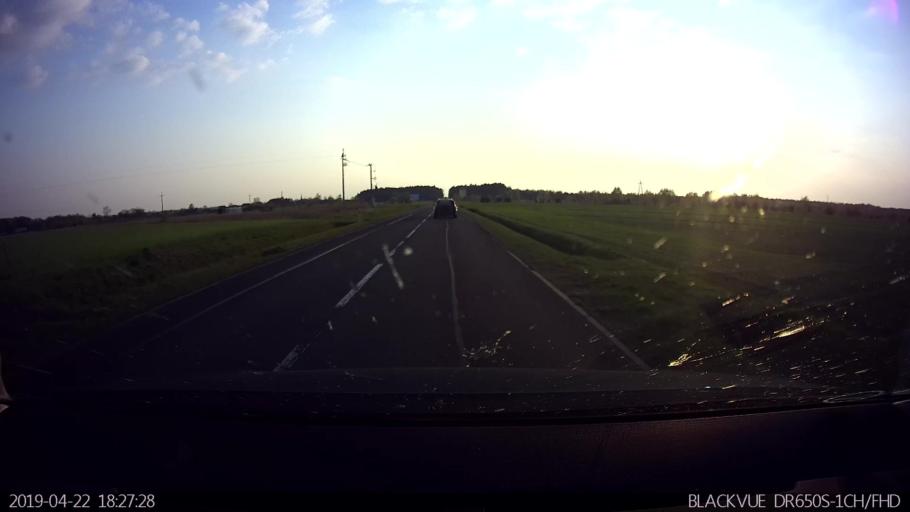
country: PL
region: Masovian Voivodeship
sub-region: Powiat wolominski
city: Tluszcz
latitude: 52.4646
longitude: 21.4959
